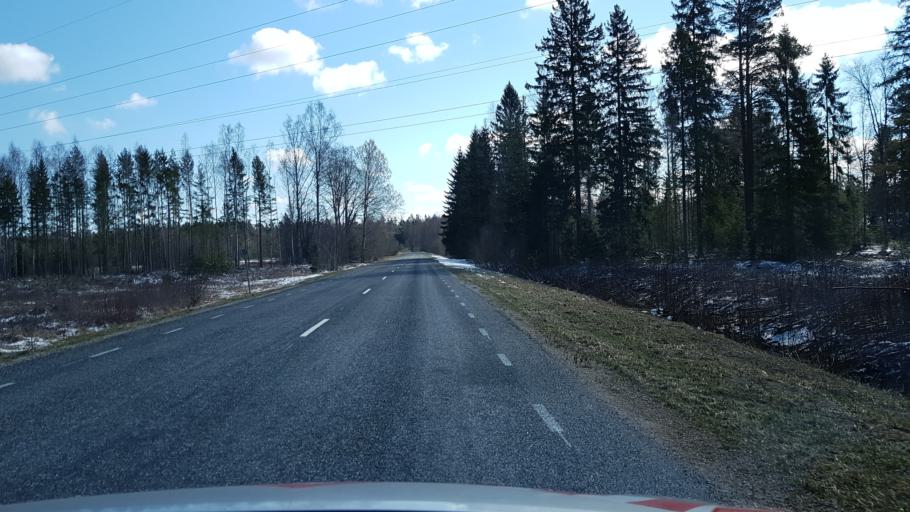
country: EE
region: Harju
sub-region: Loksa linn
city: Loksa
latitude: 59.5639
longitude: 25.9540
